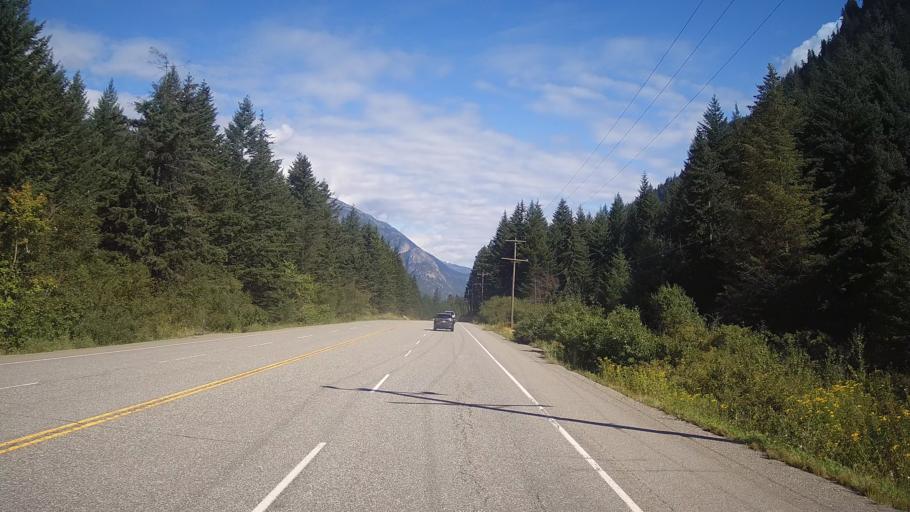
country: CA
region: British Columbia
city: Hope
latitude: 50.0439
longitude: -121.5376
